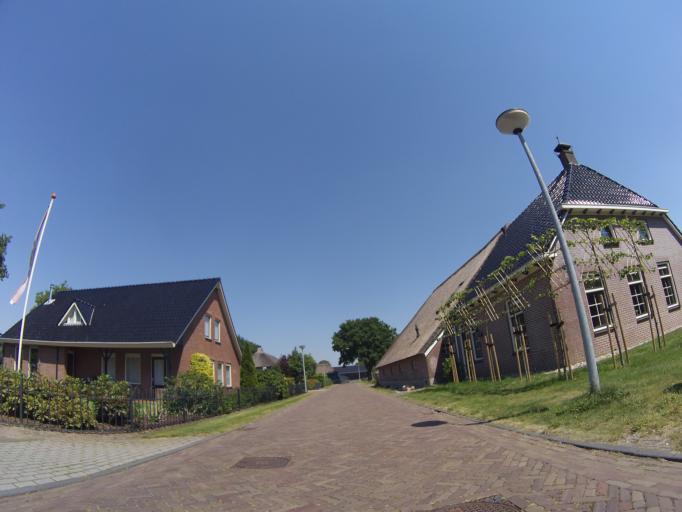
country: NL
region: Drenthe
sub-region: Gemeente Coevorden
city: Sleen
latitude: 52.7895
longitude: 6.8040
